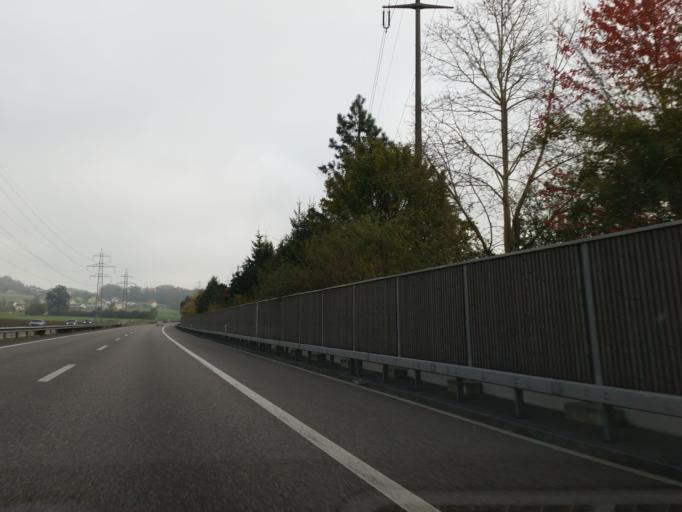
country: CH
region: Aargau
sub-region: Bezirk Zofingen
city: Oftringen
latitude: 47.3185
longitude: 7.9520
